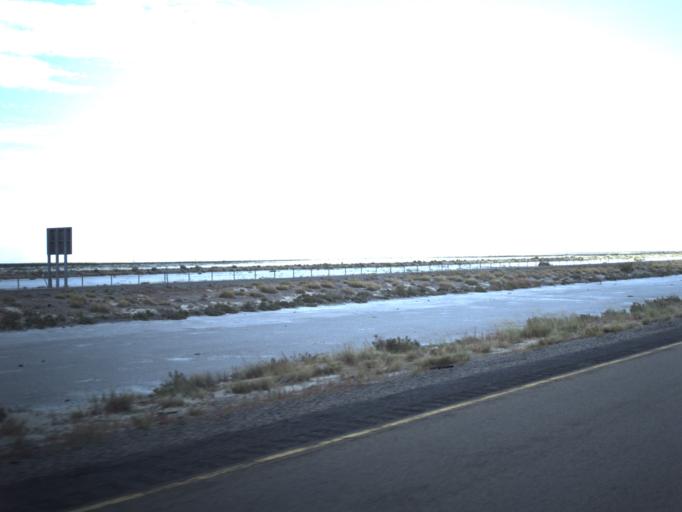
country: US
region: Utah
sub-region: Tooele County
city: Grantsville
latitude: 40.7564
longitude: -112.7611
